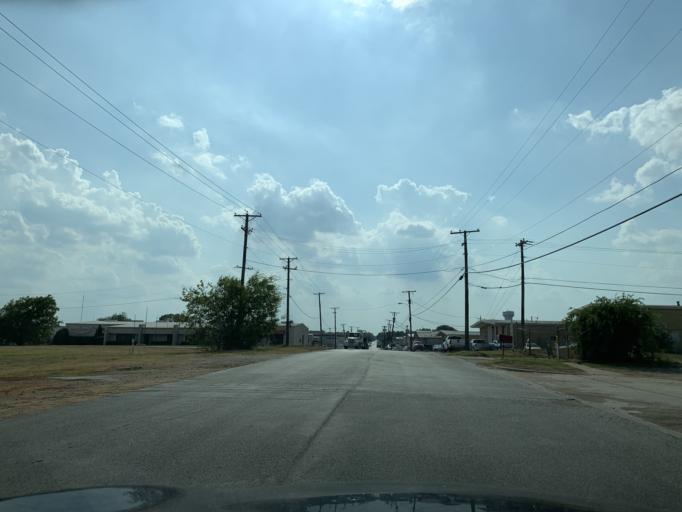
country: US
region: Texas
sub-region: Tarrant County
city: Richland Hills
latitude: 32.7948
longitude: -97.2432
